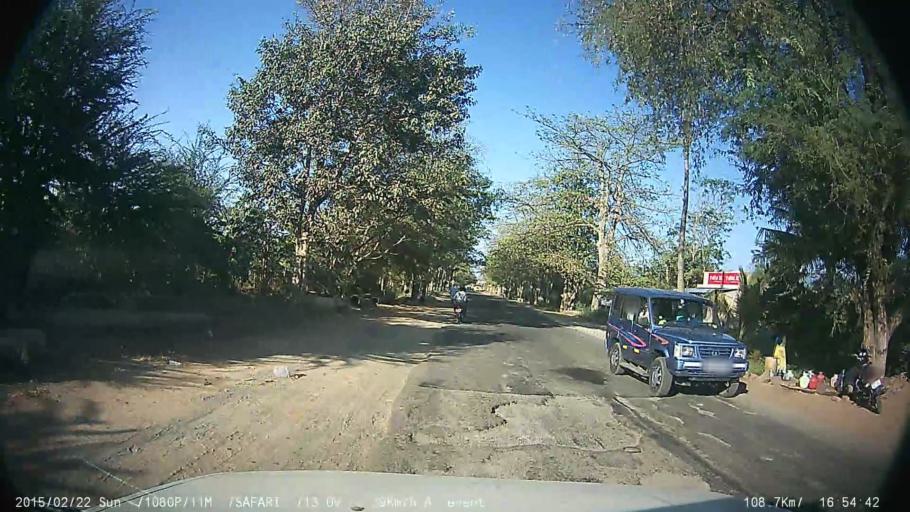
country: IN
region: Tamil Nadu
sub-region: Theni
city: Gudalur
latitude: 9.6728
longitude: 77.2381
